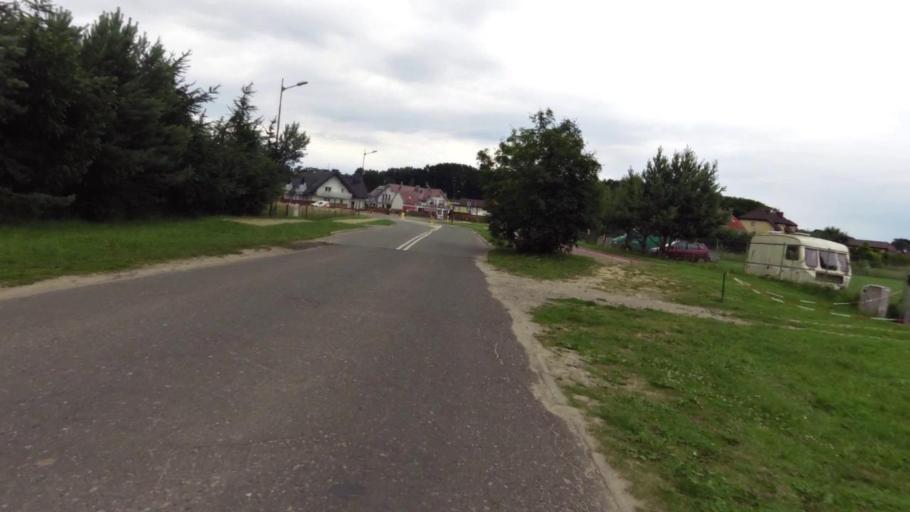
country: PL
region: West Pomeranian Voivodeship
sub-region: Powiat gryficki
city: Rewal
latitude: 54.0813
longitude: 15.0314
